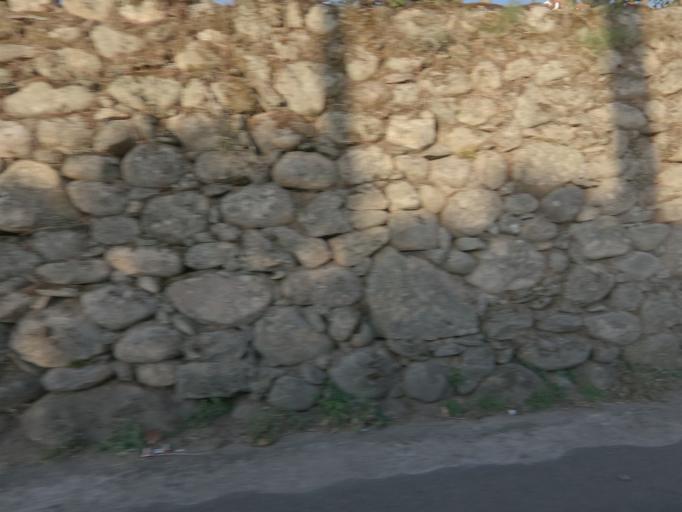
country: PT
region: Vila Real
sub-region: Vila Real
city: Vila Real
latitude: 41.3153
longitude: -7.7654
